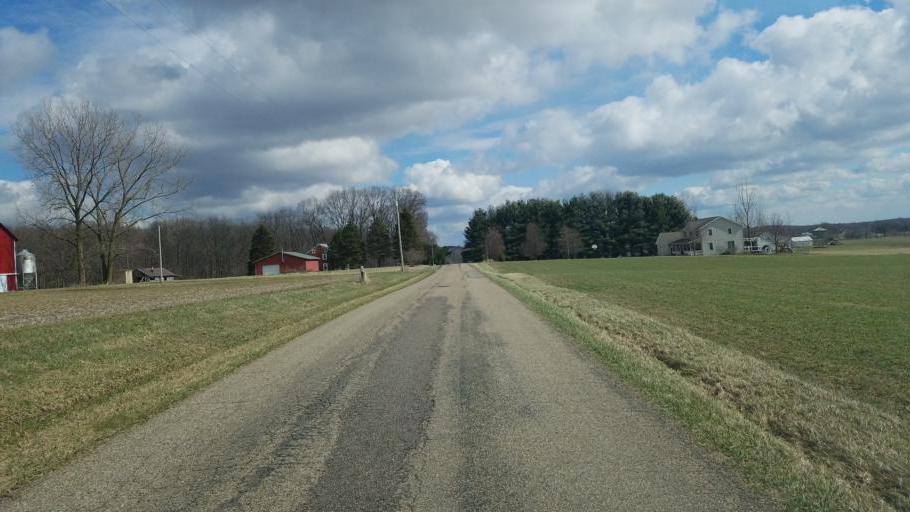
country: US
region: Ohio
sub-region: Sandusky County
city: Bellville
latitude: 40.5504
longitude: -82.5213
